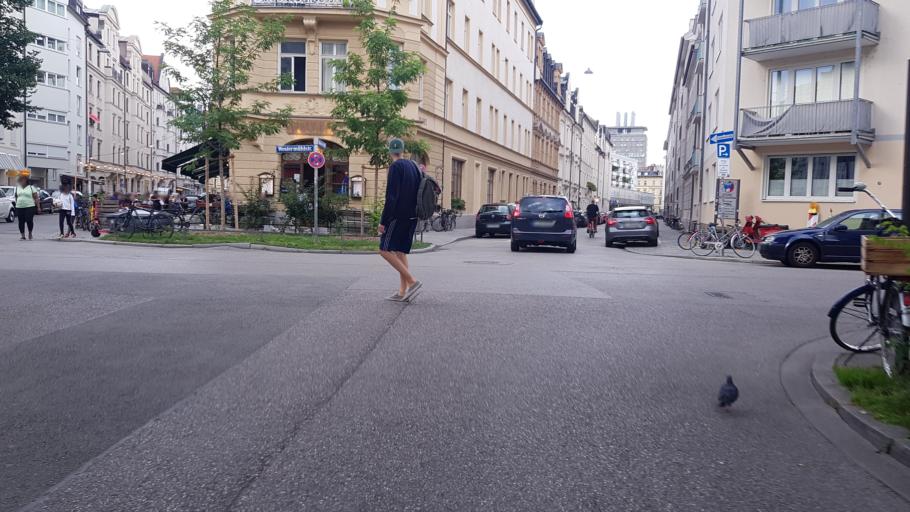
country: DE
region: Bavaria
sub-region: Upper Bavaria
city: Munich
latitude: 48.1283
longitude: 11.5696
